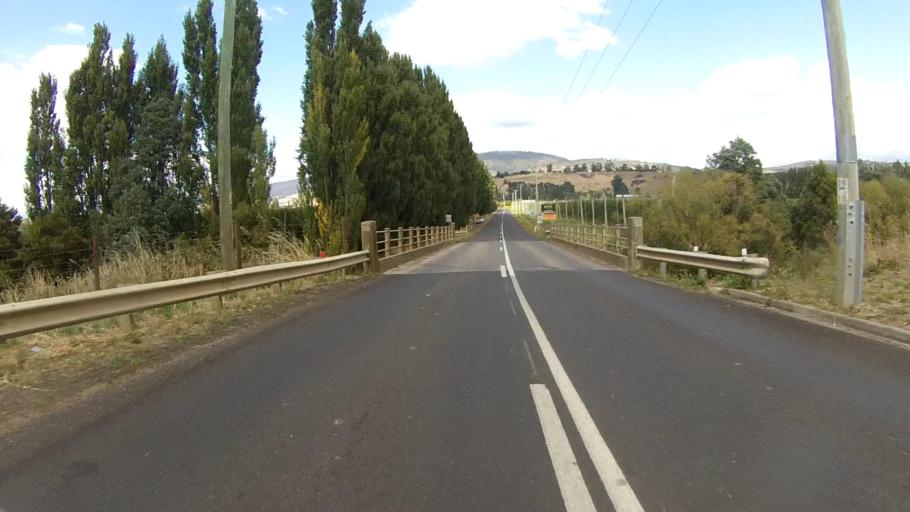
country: AU
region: Tasmania
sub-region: Derwent Valley
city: New Norfolk
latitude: -42.6991
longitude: 146.8909
